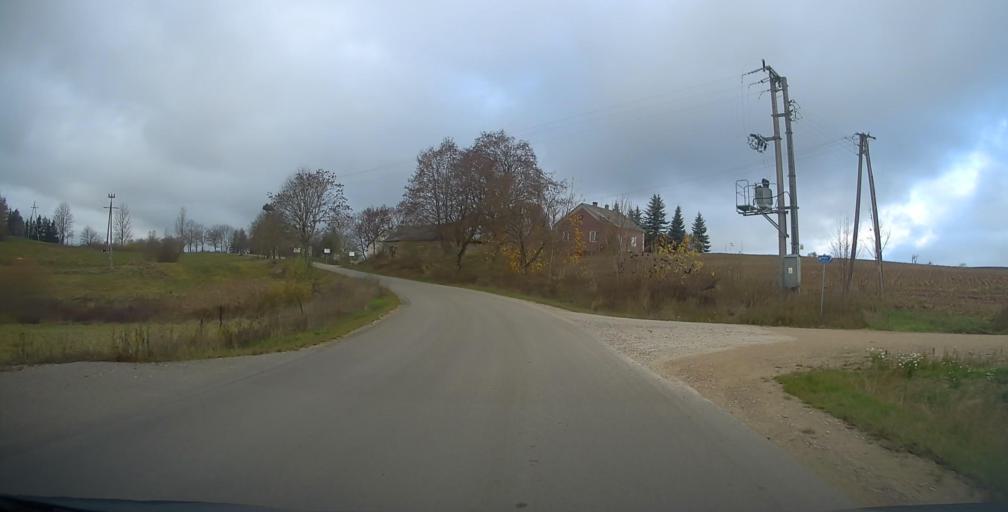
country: PL
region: Podlasie
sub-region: Suwalki
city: Suwalki
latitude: 54.3156
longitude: 22.8766
